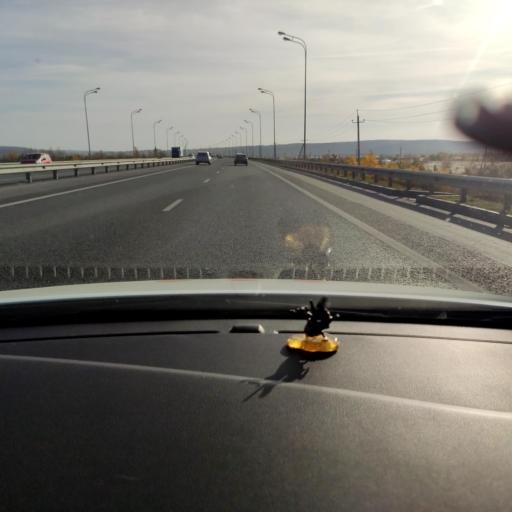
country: RU
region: Tatarstan
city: Osinovo
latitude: 55.8163
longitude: 48.8425
